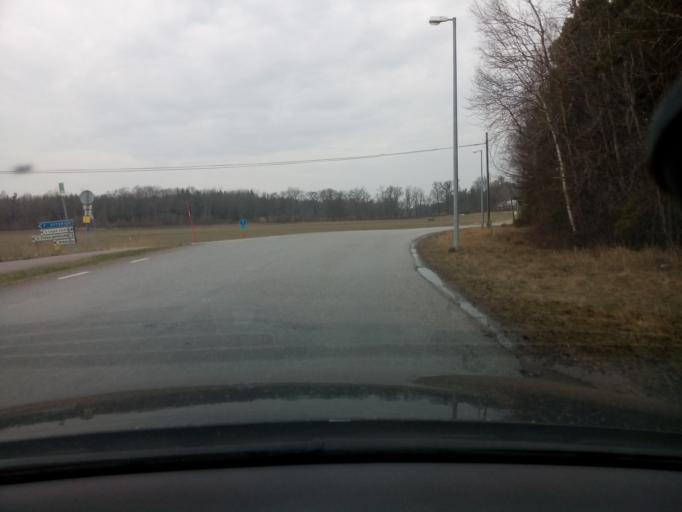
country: SE
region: Soedermanland
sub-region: Trosa Kommun
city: Trosa
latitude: 58.9037
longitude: 17.5245
